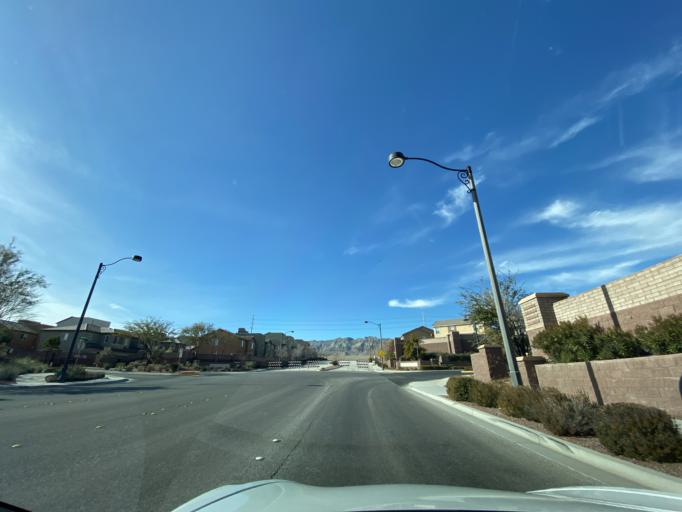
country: US
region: Nevada
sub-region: Clark County
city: Summerlin South
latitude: 36.2882
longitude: -115.3308
